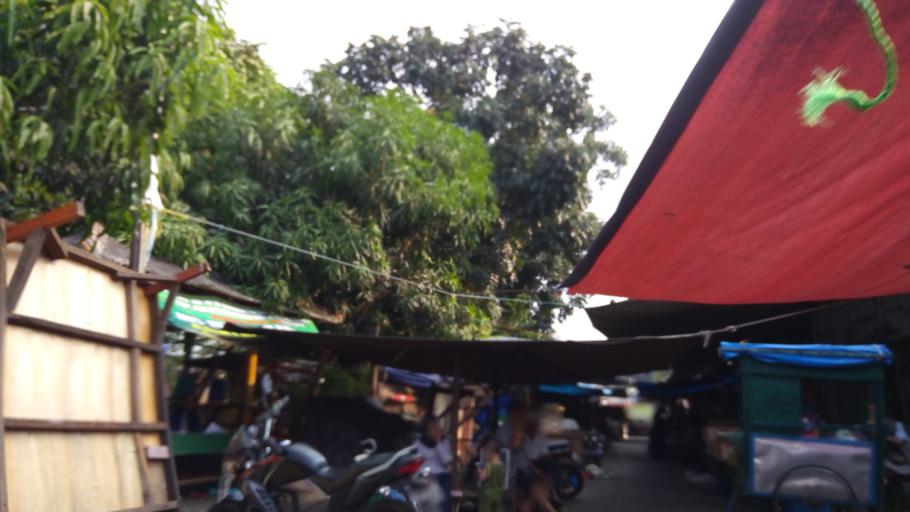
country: ID
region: Jakarta Raya
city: Jakarta
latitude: -6.1905
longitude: 106.8500
